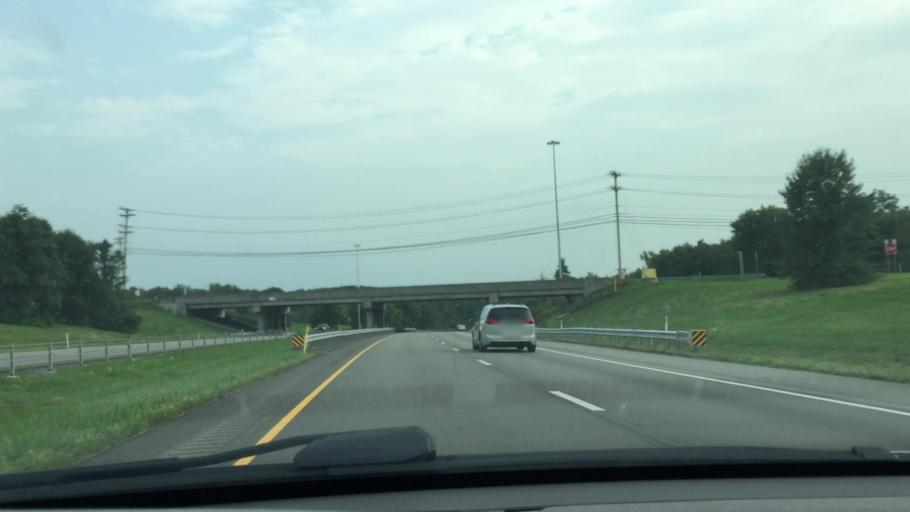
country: US
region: Pennsylvania
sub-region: Beaver County
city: Beaver
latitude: 40.6376
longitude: -80.3201
